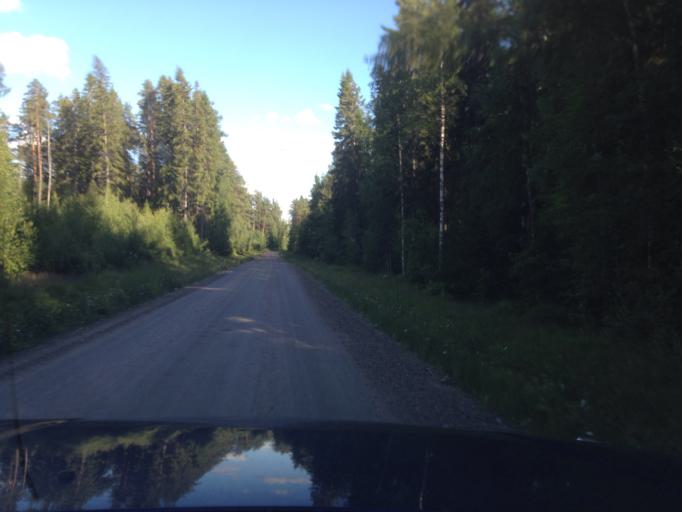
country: SE
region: Dalarna
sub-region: Ludvika Kommun
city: Abborrberget
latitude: 60.2343
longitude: 14.8075
